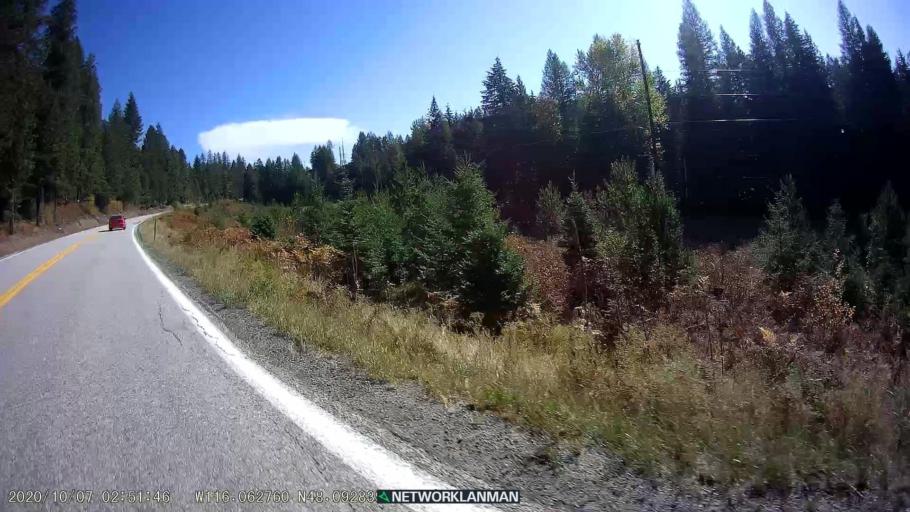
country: US
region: Idaho
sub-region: Bonner County
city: Ponderay
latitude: 48.0928
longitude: -116.0623
